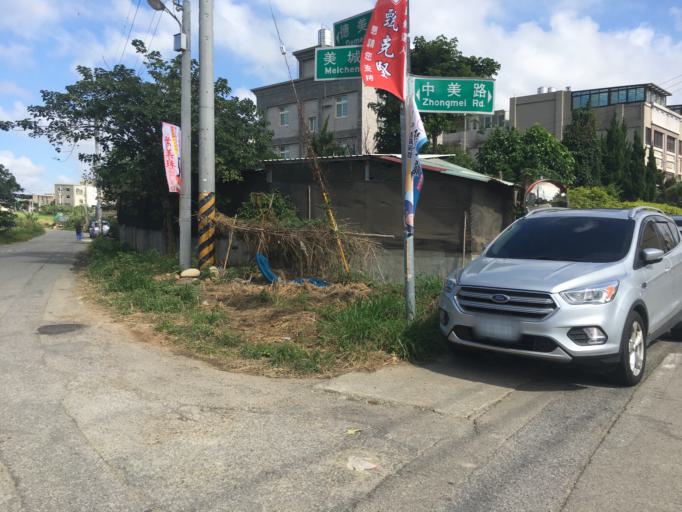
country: TW
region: Taiwan
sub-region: Hsinchu
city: Zhubei
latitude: 24.8885
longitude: 121.0493
